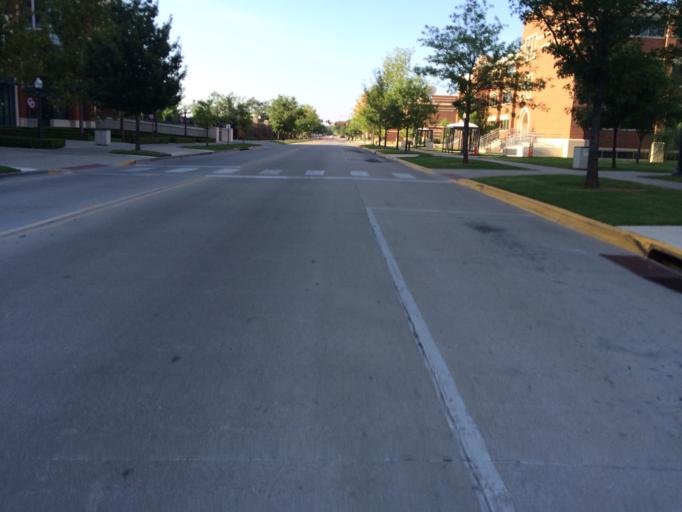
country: US
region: Oklahoma
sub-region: Cleveland County
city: Norman
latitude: 35.2060
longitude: -97.4443
